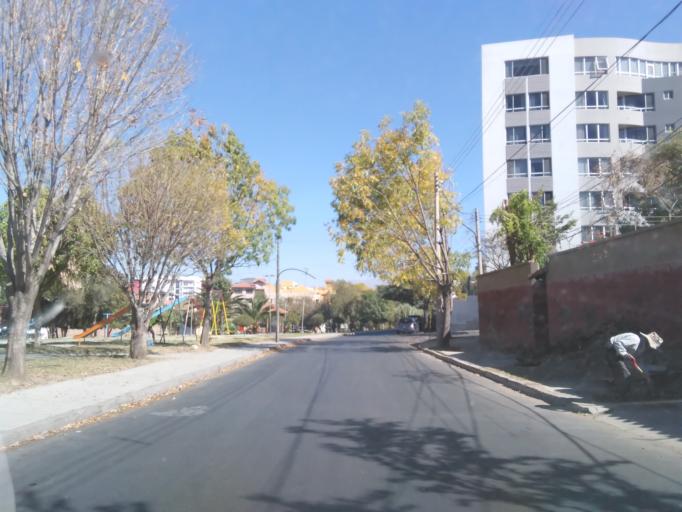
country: BO
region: Cochabamba
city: Cochabamba
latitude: -17.3706
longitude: -66.1518
